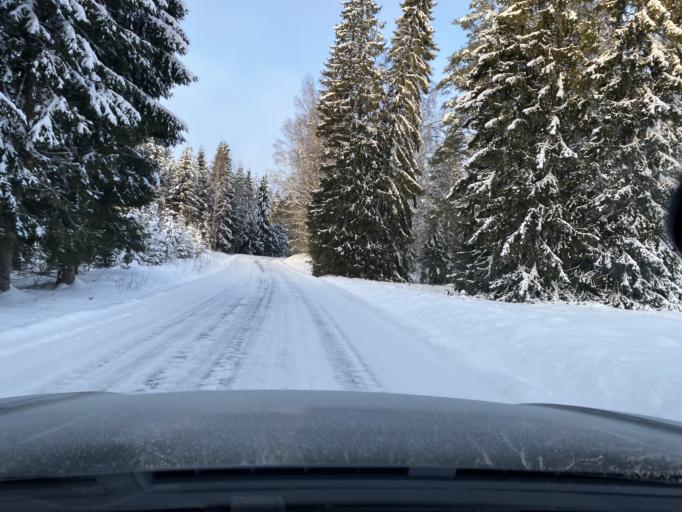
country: FI
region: Haeme
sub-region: Forssa
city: Tammela
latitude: 60.8629
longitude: 23.8920
